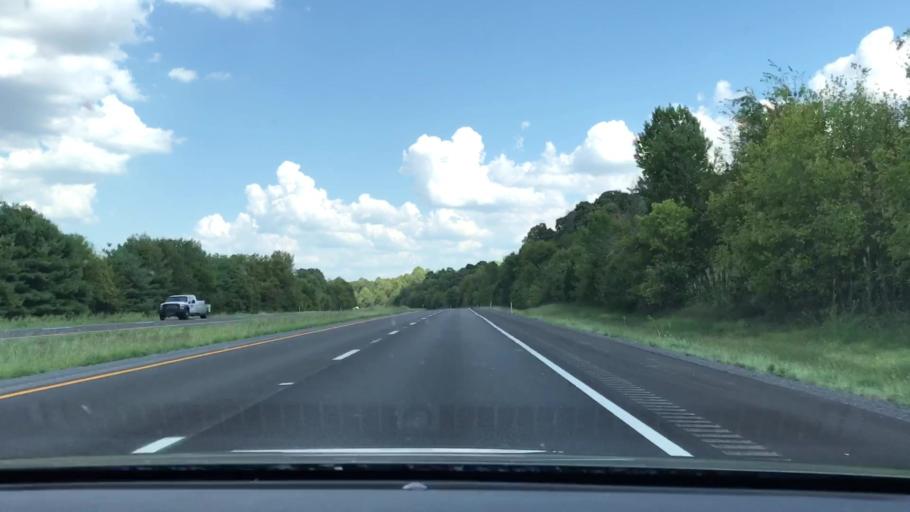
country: US
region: Kentucky
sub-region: Lyon County
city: Eddyville
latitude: 37.0943
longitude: -88.0466
